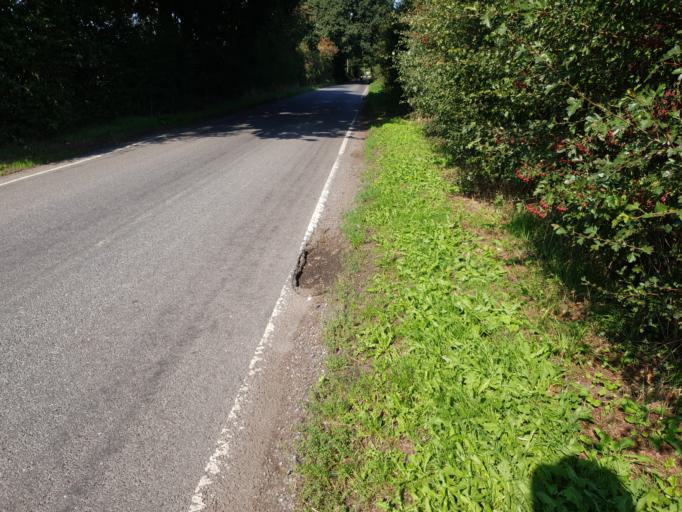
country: GB
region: England
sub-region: Suffolk
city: East Bergholt
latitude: 51.9379
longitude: 0.9940
